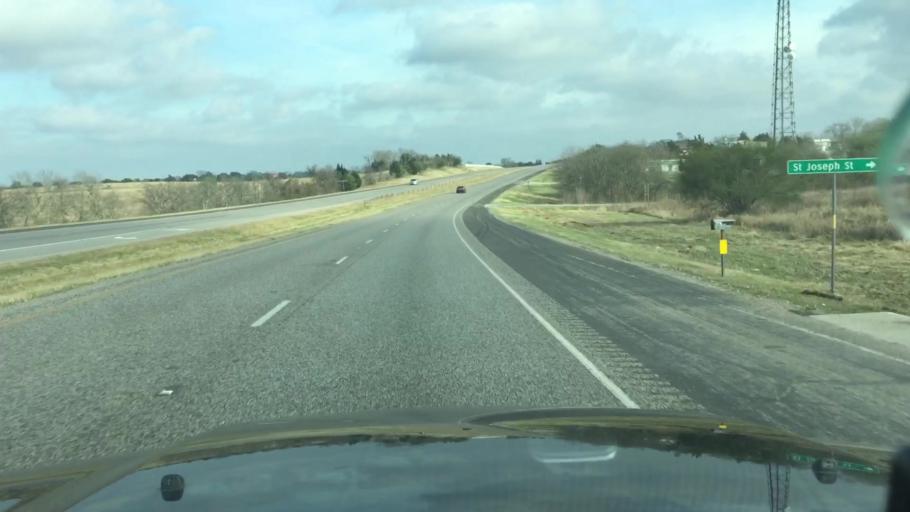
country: US
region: Texas
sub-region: Washington County
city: Brenham
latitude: 30.1354
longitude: -96.2528
